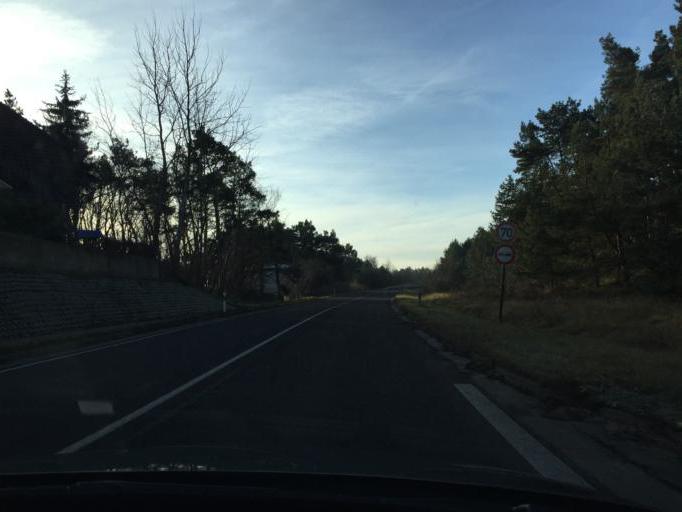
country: DE
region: Brandenburg
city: Ziltendorf
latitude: 52.2055
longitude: 14.6179
